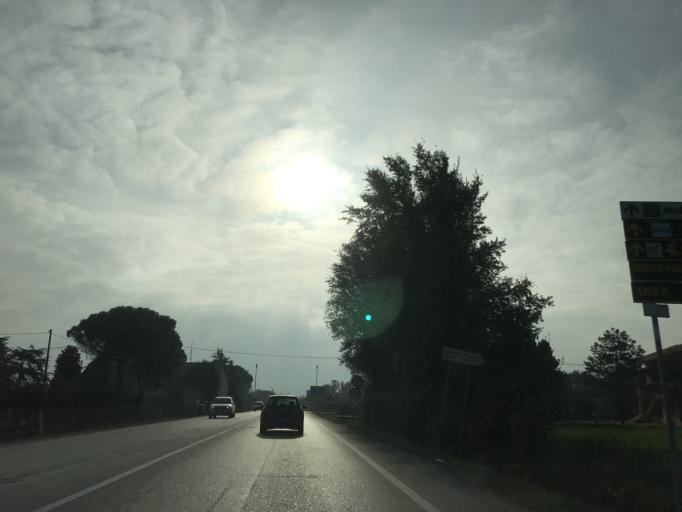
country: IT
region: Emilia-Romagna
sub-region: Provincia di Rimini
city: Santa Giustina
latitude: 44.1046
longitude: 12.4887
